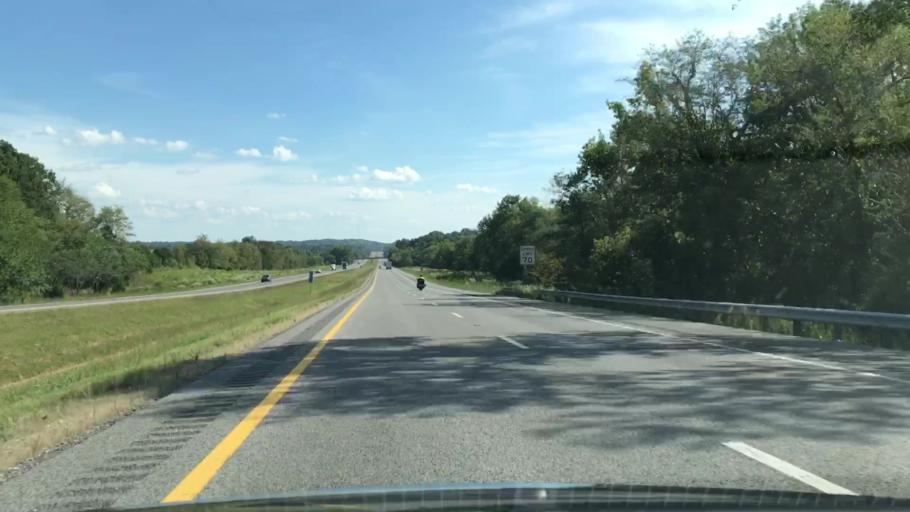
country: US
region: Alabama
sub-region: Limestone County
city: Ardmore
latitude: 35.0714
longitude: -86.8827
